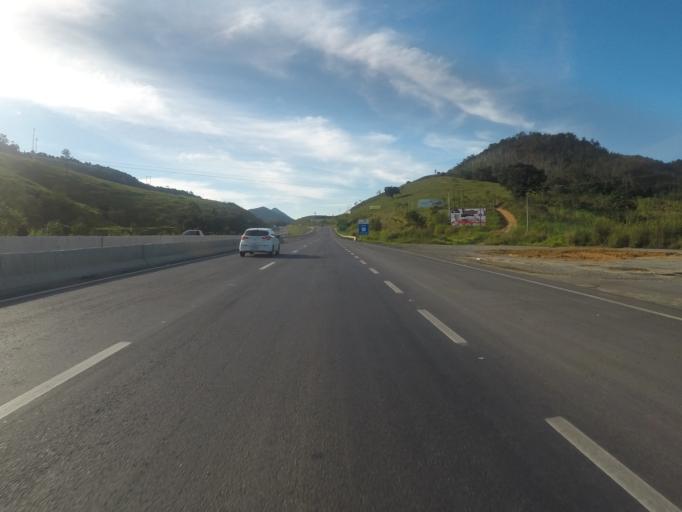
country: BR
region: Espirito Santo
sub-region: Ibiracu
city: Ibiracu
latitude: -19.8627
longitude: -40.3828
